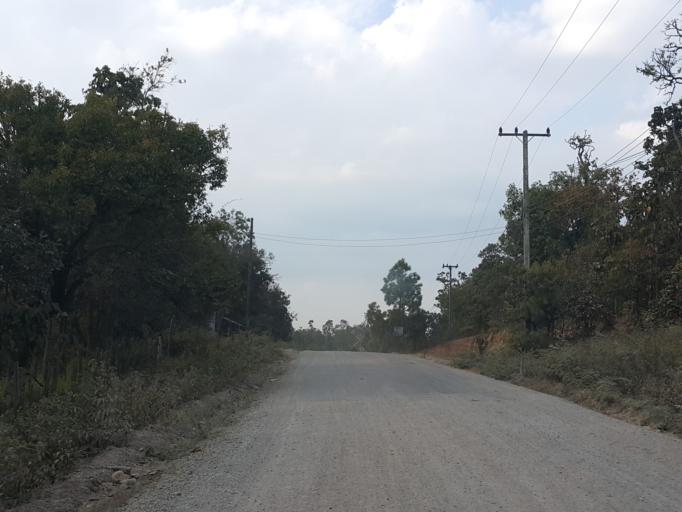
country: TH
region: Chiang Mai
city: Om Koi
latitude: 17.8080
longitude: 98.3323
